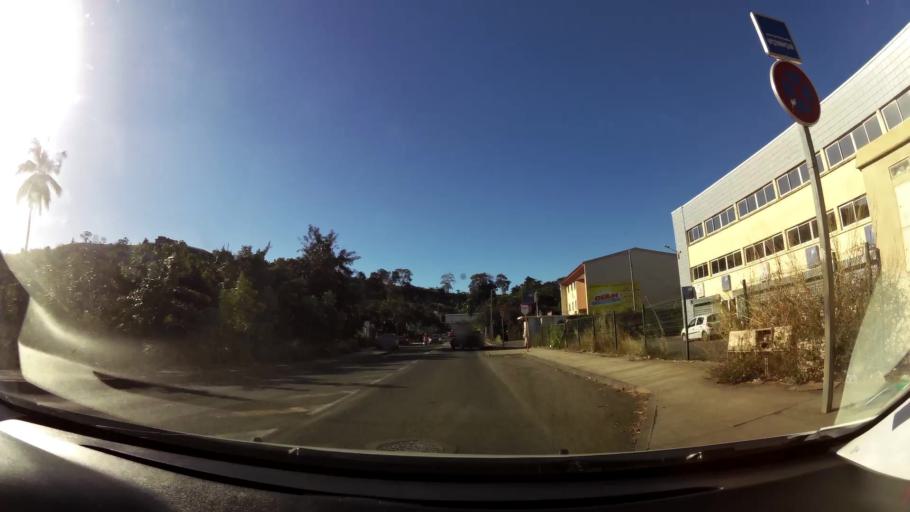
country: YT
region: Mamoudzou
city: Mamoudzou
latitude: -12.7620
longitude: 45.2262
